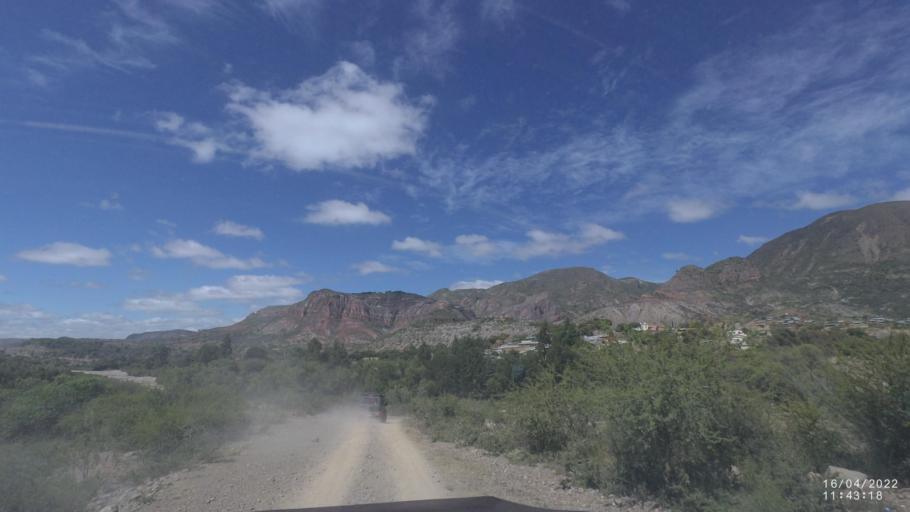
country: BO
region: Cochabamba
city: Mizque
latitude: -17.9810
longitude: -65.6283
